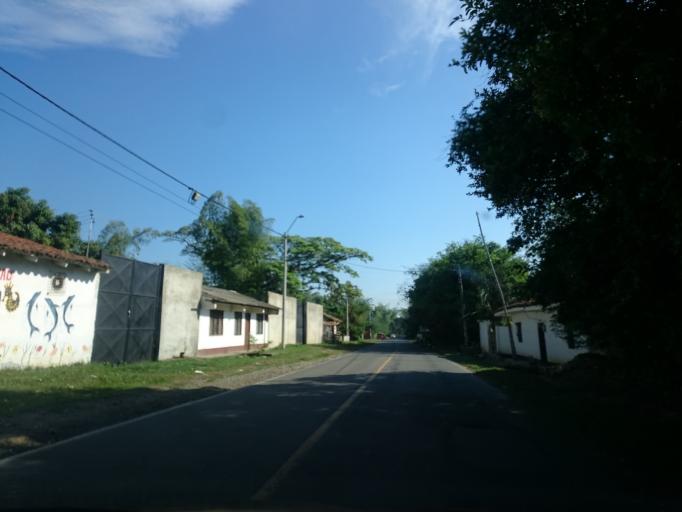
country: CO
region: Cauca
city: Santander de Quilichao
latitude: 3.0264
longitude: -76.4770
